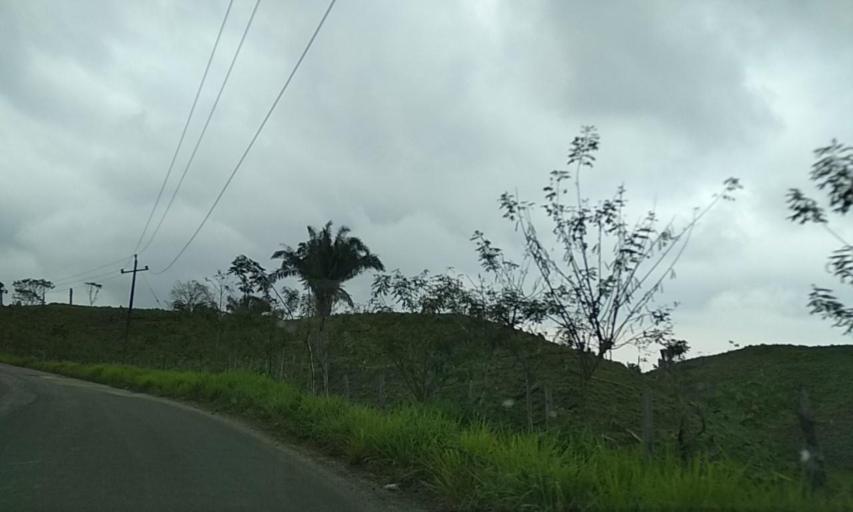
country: MX
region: Tabasco
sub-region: Huimanguillo
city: Francisco Rueda
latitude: 17.6420
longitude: -94.0924
